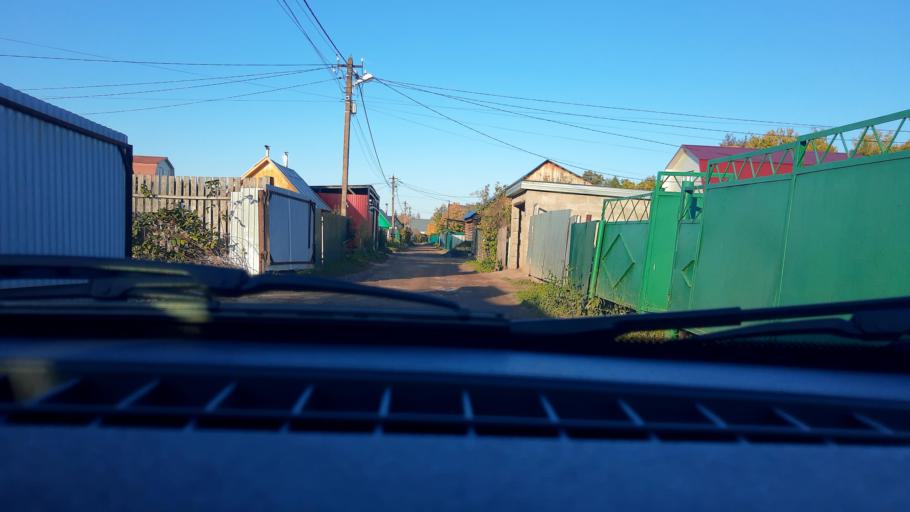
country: RU
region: Bashkortostan
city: Mikhaylovka
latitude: 54.7816
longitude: 55.8075
